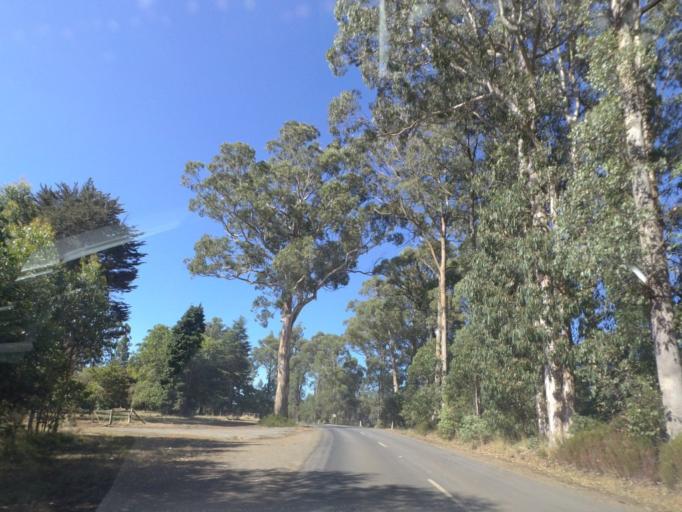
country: AU
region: Victoria
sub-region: Murrindindi
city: Kinglake West
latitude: -37.4919
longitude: 145.3215
